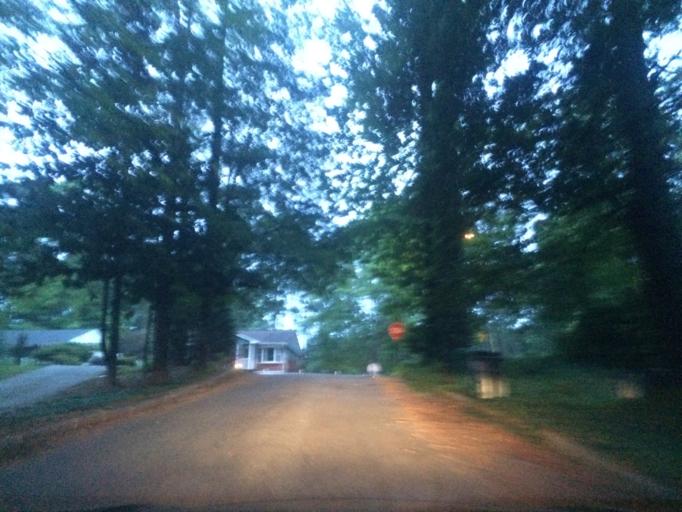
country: US
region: Georgia
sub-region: DeKalb County
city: Druid Hills
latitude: 33.8098
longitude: -84.3482
